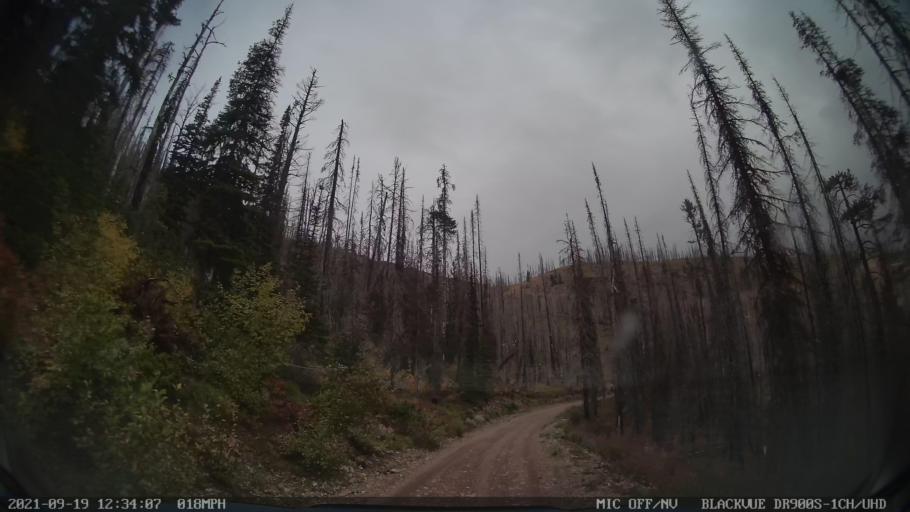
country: US
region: Montana
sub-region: Missoula County
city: Seeley Lake
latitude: 47.1878
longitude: -113.3487
